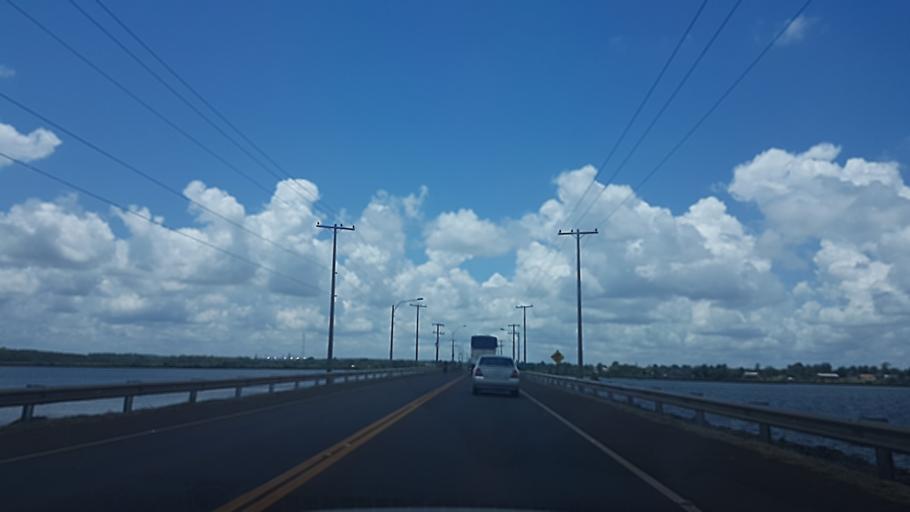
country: PY
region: Itapua
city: Carmen del Parana
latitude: -27.2121
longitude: -56.1567
